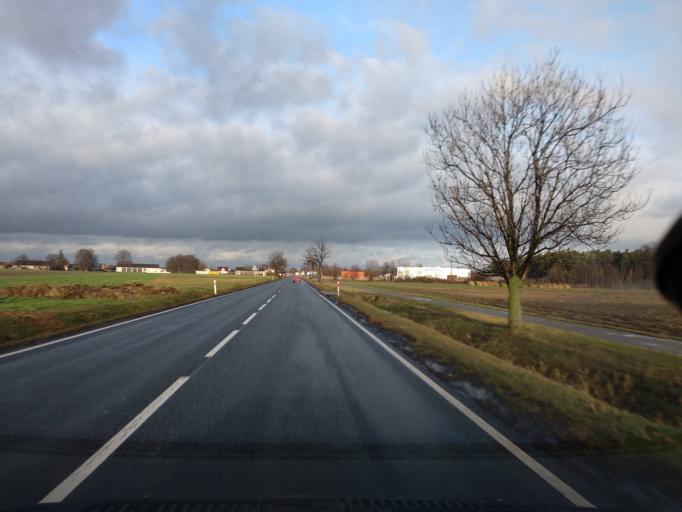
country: PL
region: Greater Poland Voivodeship
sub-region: Powiat koninski
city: Rychwal
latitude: 52.0903
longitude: 18.1645
